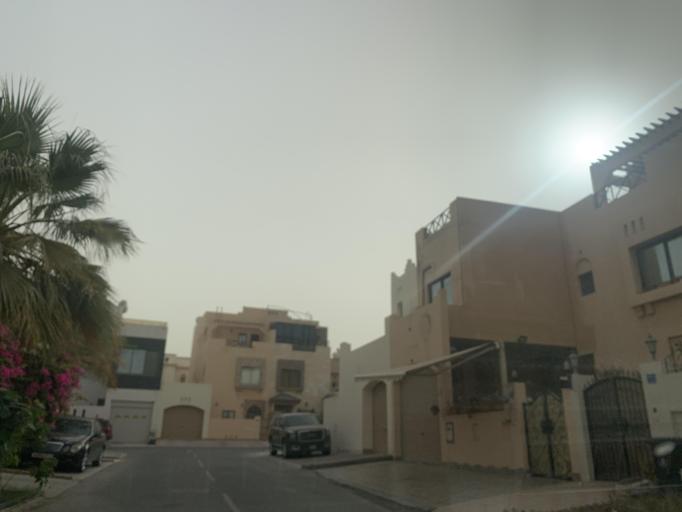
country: BH
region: Northern
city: Ar Rifa'
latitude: 26.1543
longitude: 50.5739
